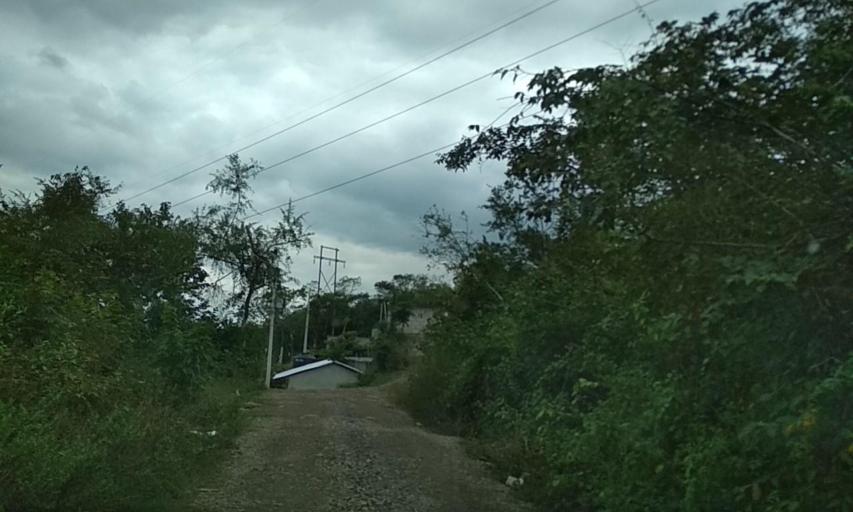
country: MX
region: Veracruz
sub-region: Papantla
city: El Chote
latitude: 20.4000
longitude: -97.3385
